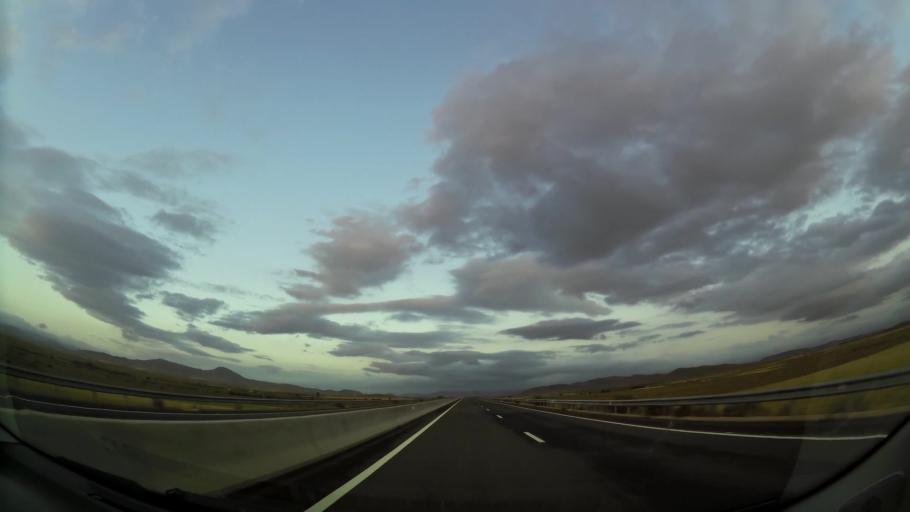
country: MA
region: Oriental
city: El Aioun
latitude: 34.6032
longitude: -2.7449
